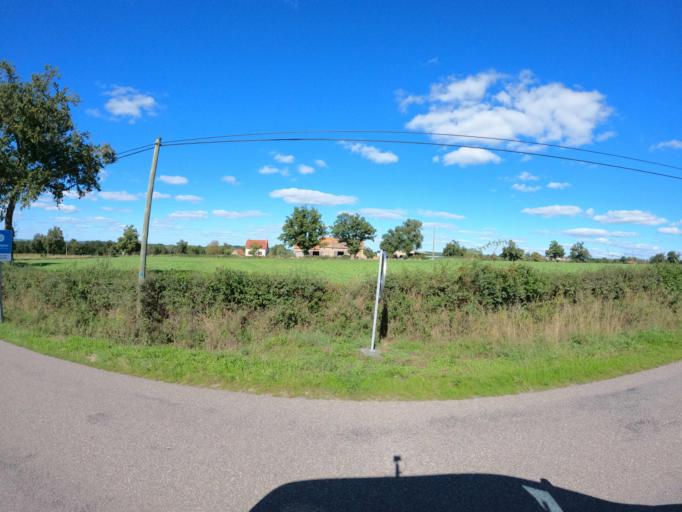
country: FR
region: Auvergne
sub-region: Departement de l'Allier
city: Buxieres-les-Mines
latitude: 46.4044
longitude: 2.9151
